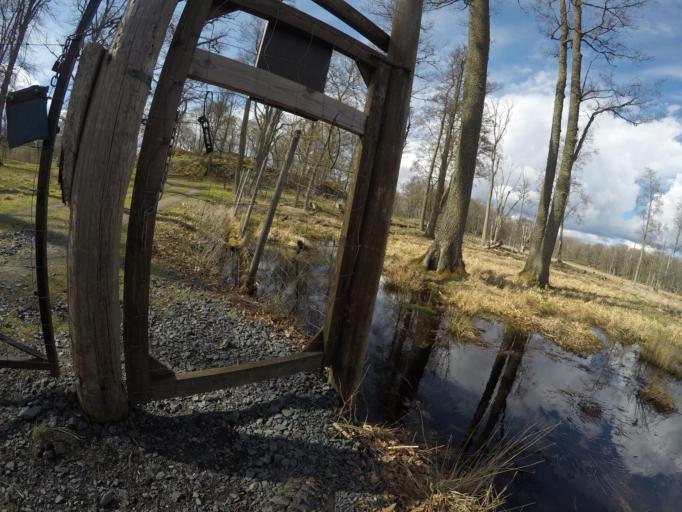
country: SE
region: Vaestmanland
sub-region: Kungsors Kommun
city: Kungsoer
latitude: 59.2722
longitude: 16.1289
